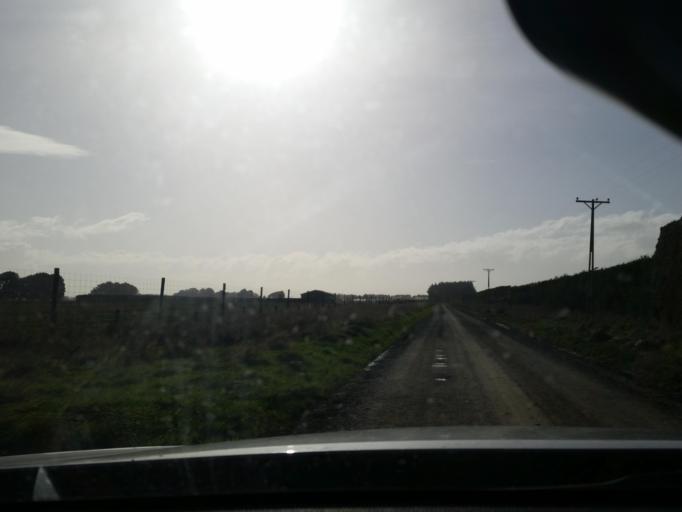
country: NZ
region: Southland
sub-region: Invercargill City
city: Invercargill
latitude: -46.2891
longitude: 168.2946
